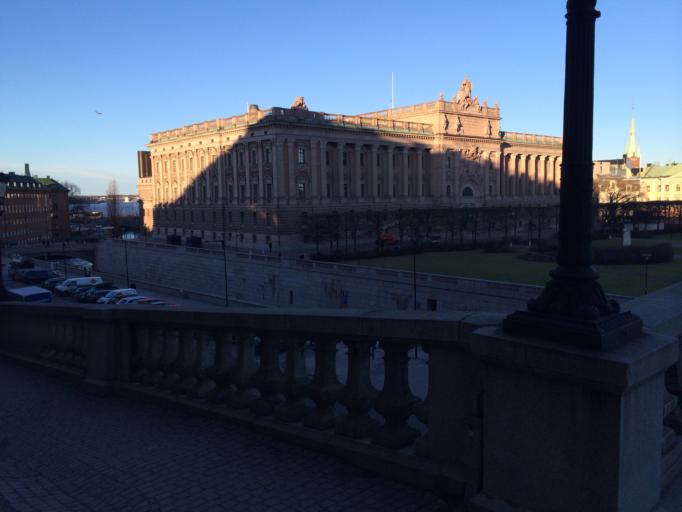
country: SE
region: Stockholm
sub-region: Stockholms Kommun
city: Stockholm
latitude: 59.3273
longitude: 18.0710
